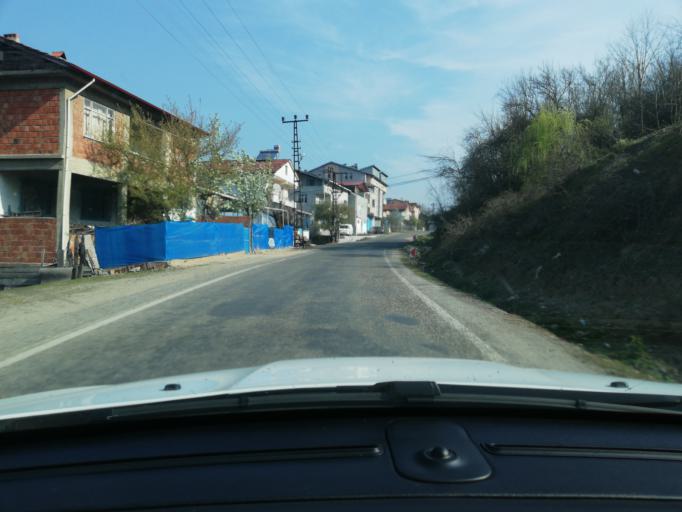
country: TR
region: Karabuk
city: Yenice
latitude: 41.2526
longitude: 32.3584
